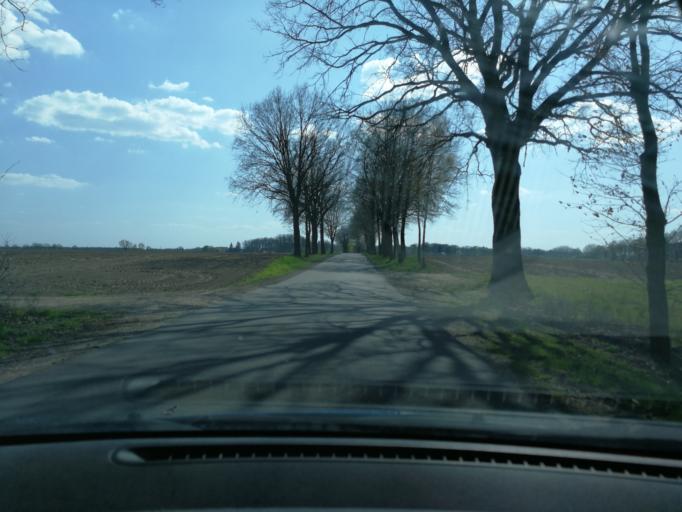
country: DE
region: Lower Saxony
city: Reinstorf
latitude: 53.2102
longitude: 10.5857
